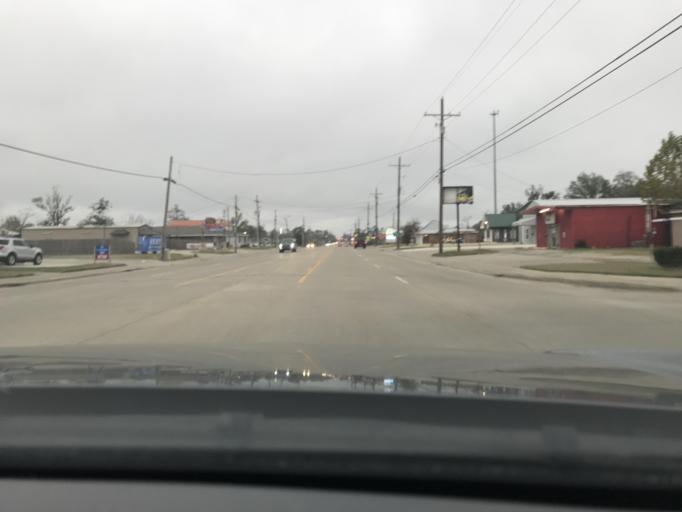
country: US
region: Louisiana
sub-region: Calcasieu Parish
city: Westlake
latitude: 30.2588
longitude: -93.2581
